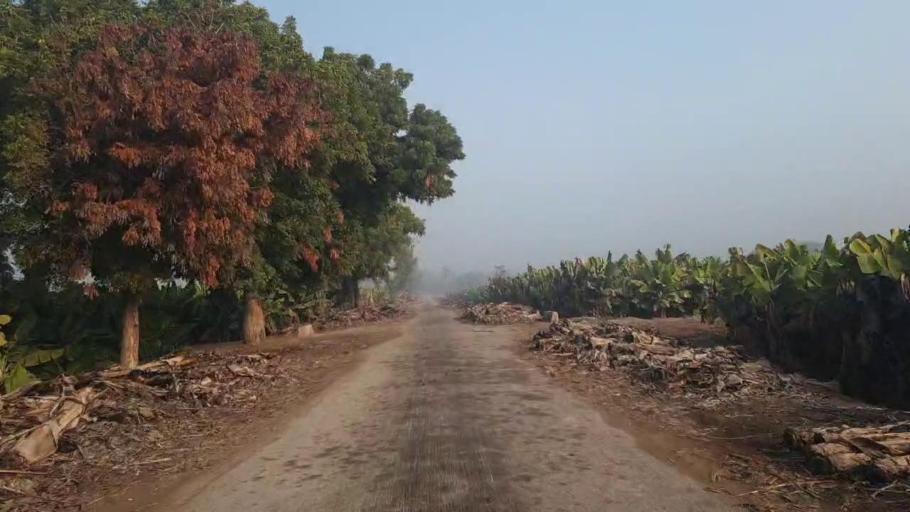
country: PK
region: Sindh
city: Tando Adam
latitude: 25.8061
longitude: 68.6333
